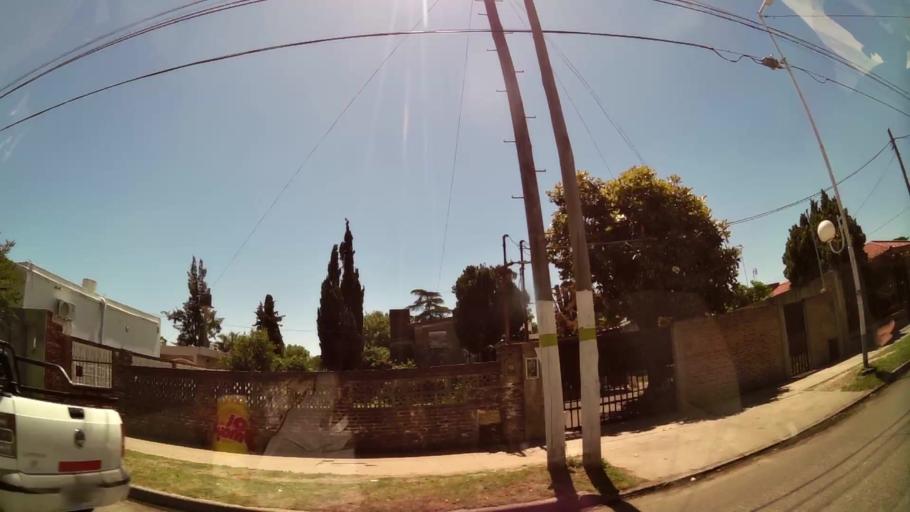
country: AR
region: Buenos Aires
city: Hurlingham
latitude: -34.5008
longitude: -58.6796
